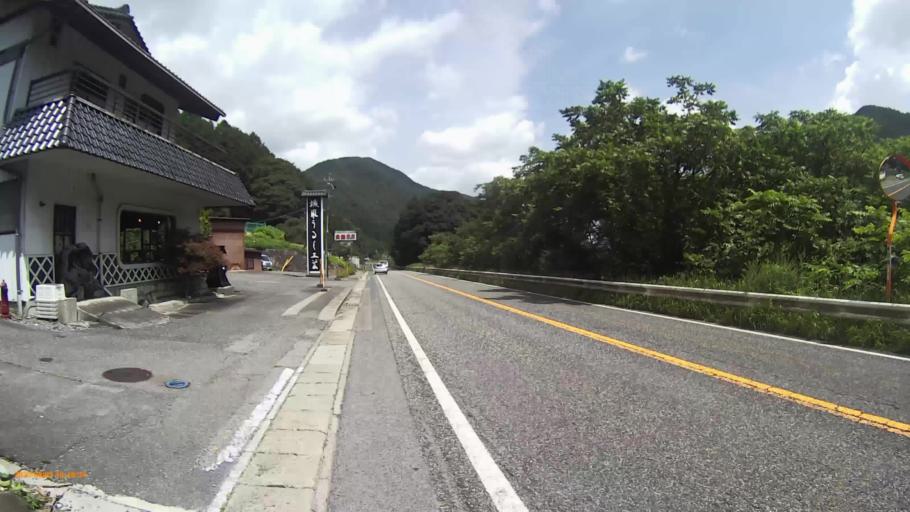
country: JP
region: Nagano
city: Tatsuno
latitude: 36.0034
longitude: 137.8551
